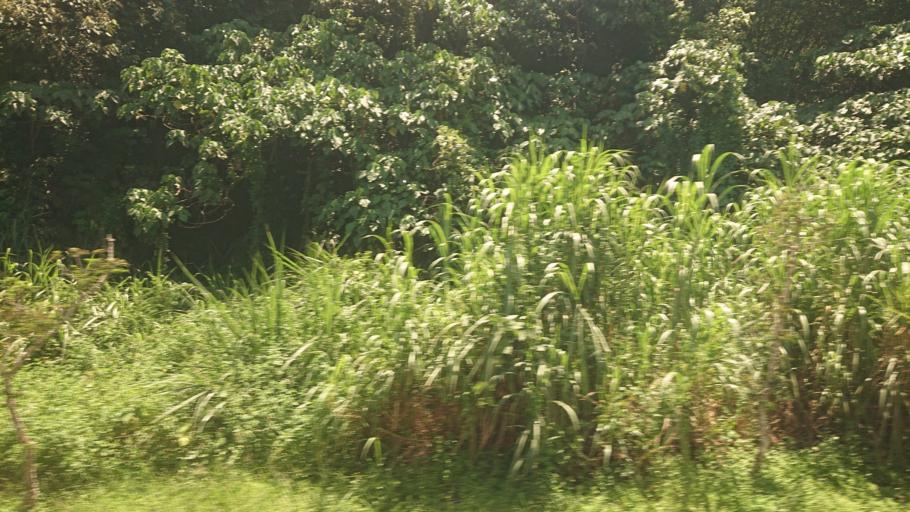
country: TW
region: Taiwan
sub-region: Nantou
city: Puli
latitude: 24.0560
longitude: 120.9348
